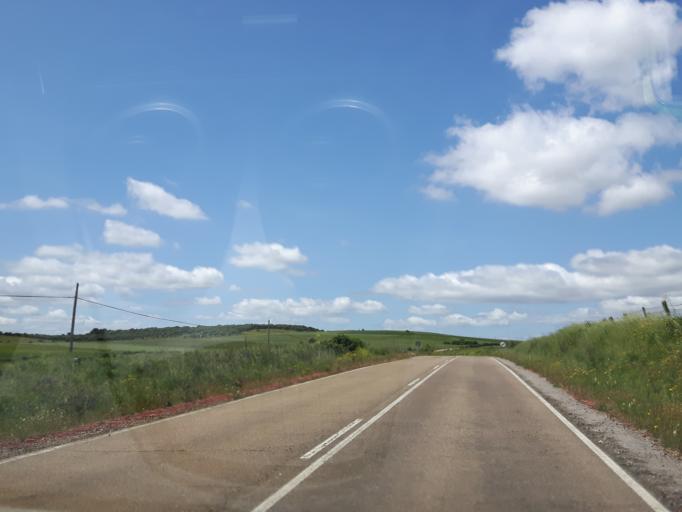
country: ES
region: Castille and Leon
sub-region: Provincia de Salamanca
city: Villar de Ciervo
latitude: 40.7296
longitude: -6.7494
